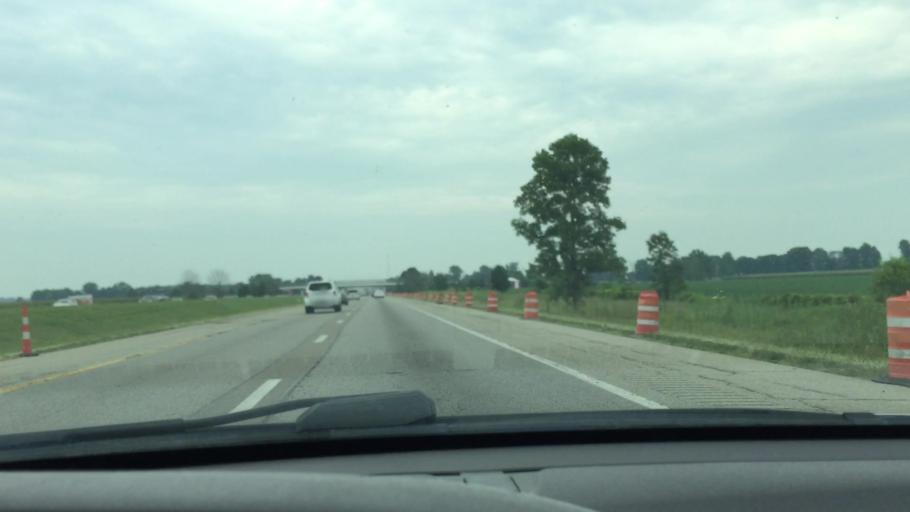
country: US
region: Ohio
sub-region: Warren County
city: Waynesville
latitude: 39.4460
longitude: -84.0319
